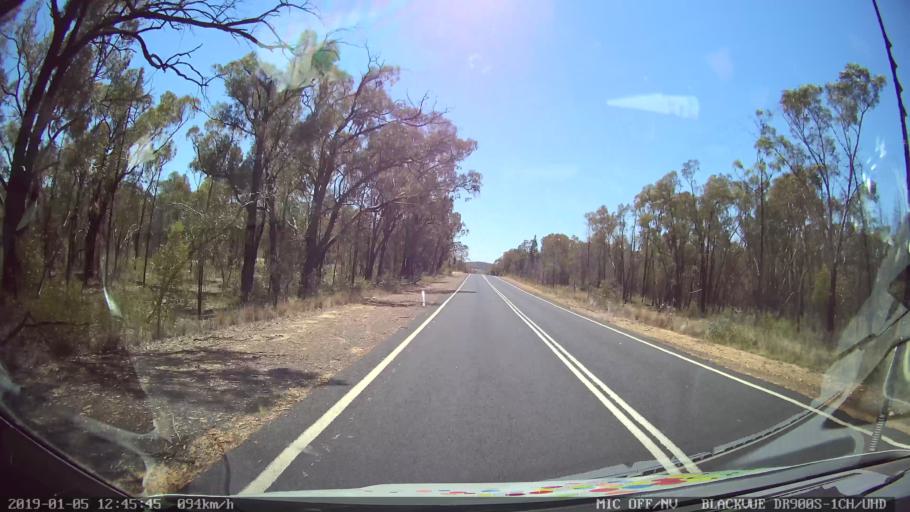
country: AU
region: New South Wales
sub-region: Warrumbungle Shire
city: Coonabarabran
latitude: -31.1248
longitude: 149.5538
